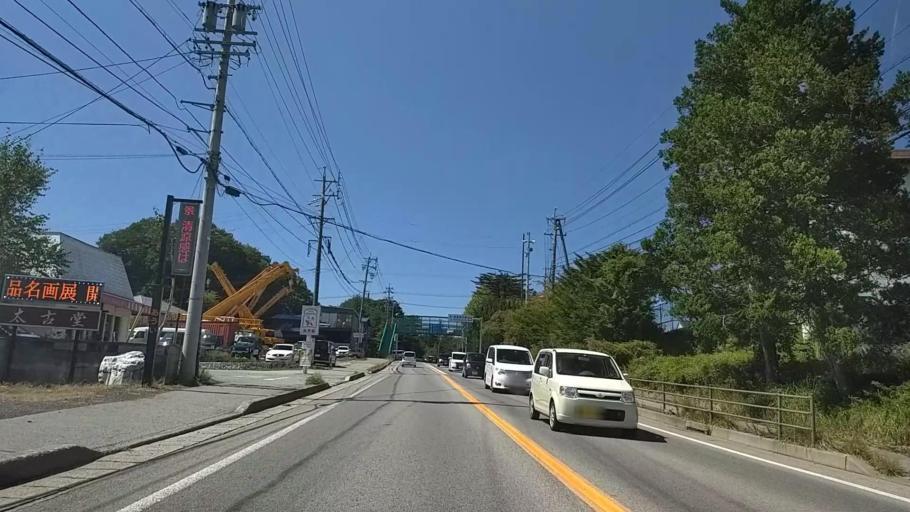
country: JP
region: Nagano
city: Komoro
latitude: 36.3420
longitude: 138.5547
